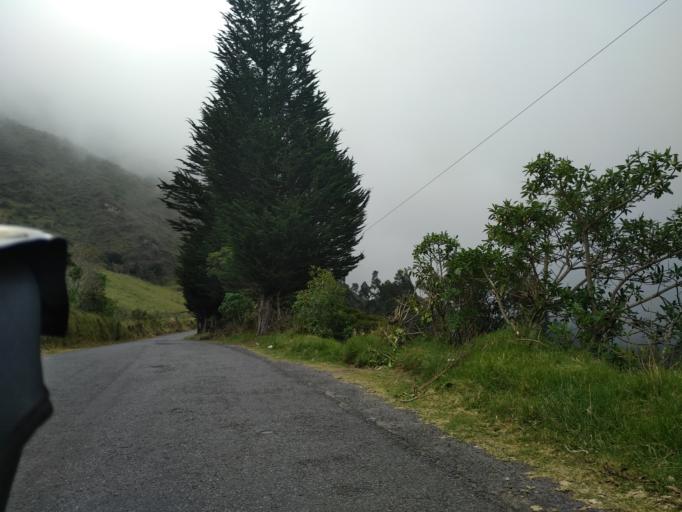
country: EC
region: Cotopaxi
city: Saquisili
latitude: -0.6911
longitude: -78.8251
